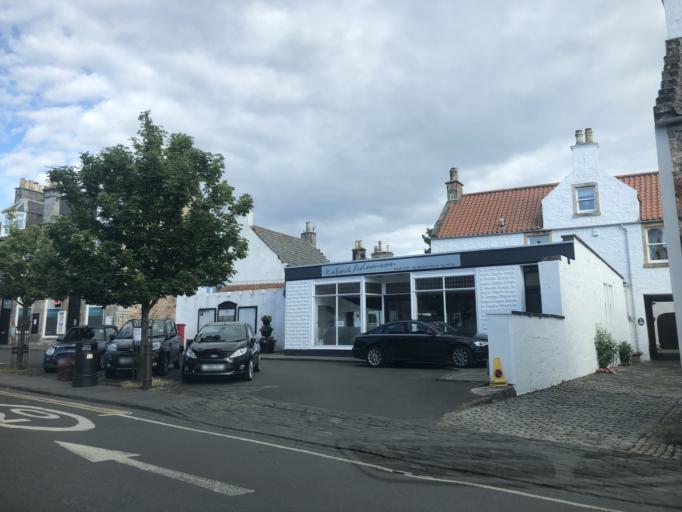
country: GB
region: Scotland
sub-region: Fife
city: Pittenweem
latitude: 56.2129
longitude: -2.7310
